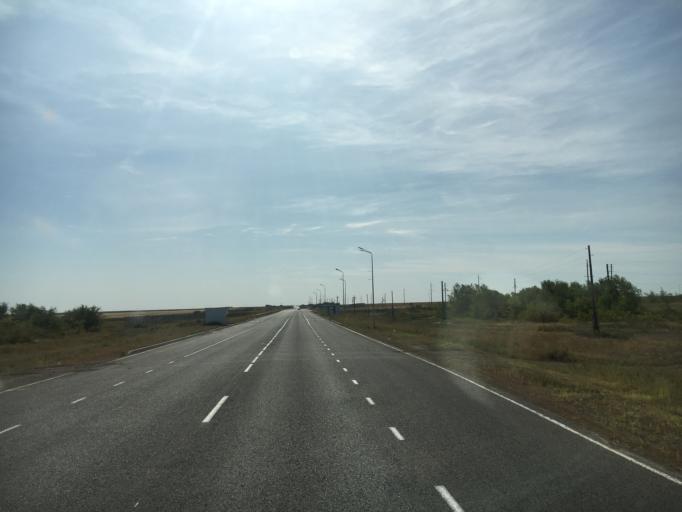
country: KZ
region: Batys Qazaqstan
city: Peremetnoe
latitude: 51.1357
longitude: 50.9086
